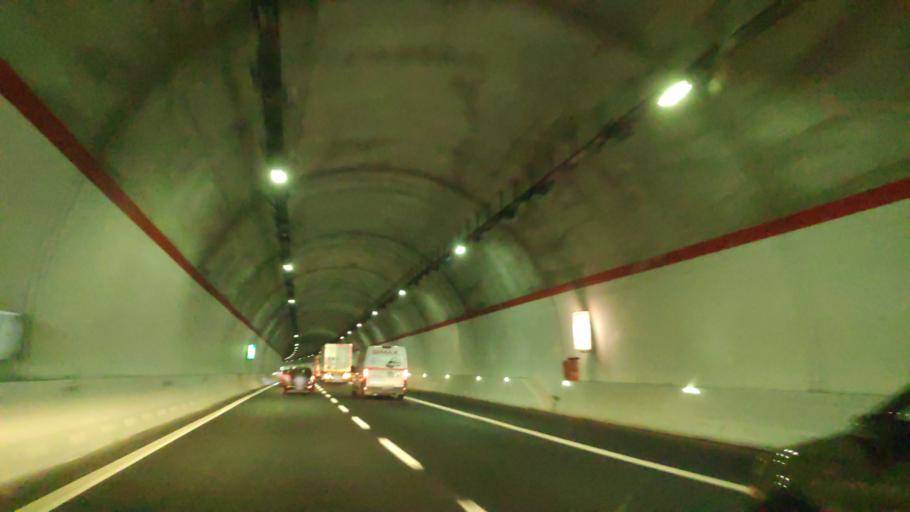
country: IT
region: Campania
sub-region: Provincia di Salerno
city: Casalbuono
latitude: 40.1879
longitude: 15.7077
